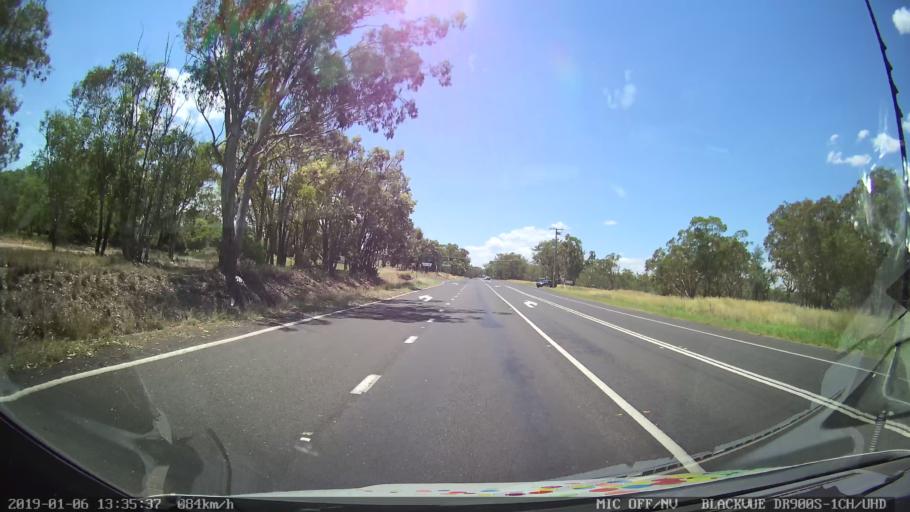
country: AU
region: New South Wales
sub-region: Tamworth Municipality
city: Kootingal
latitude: -31.0752
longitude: 151.0269
